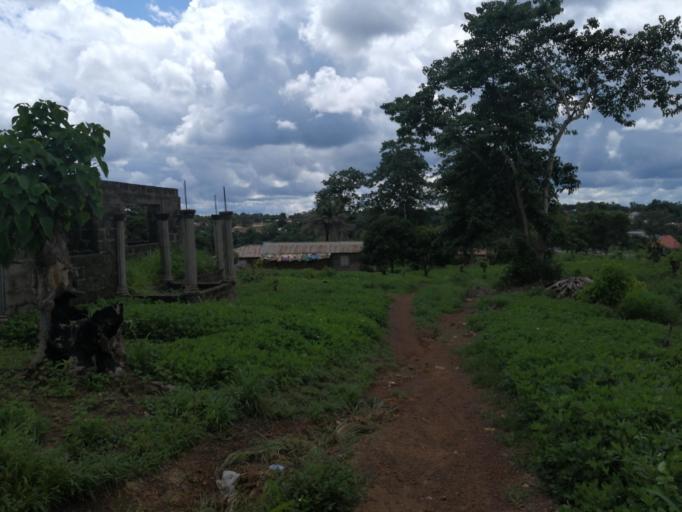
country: SL
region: Northern Province
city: Port Loko
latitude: 8.7738
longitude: -12.7763
